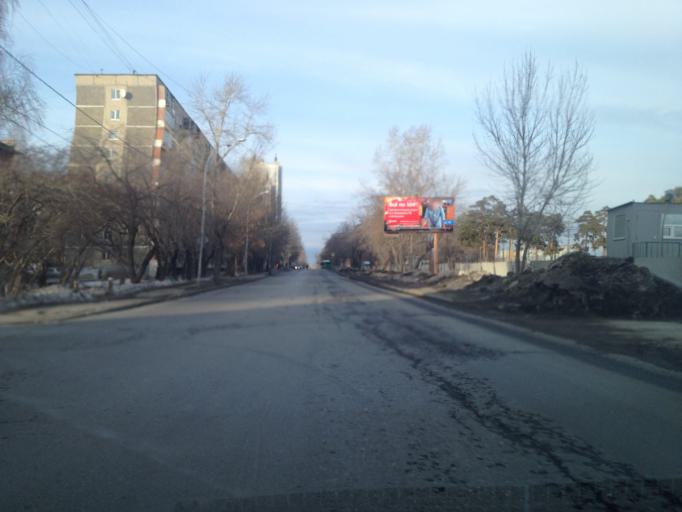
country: RU
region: Sverdlovsk
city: Sovkhoznyy
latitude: 56.7601
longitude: 60.6115
